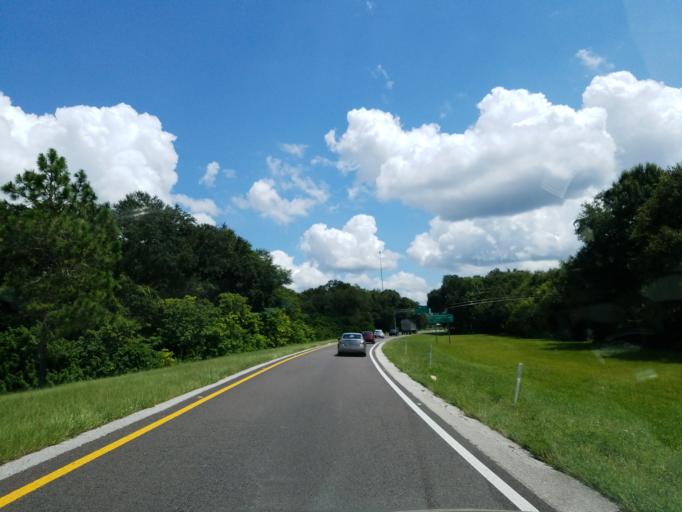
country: US
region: Florida
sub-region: Hillsborough County
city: Mango
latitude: 28.0006
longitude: -82.3318
